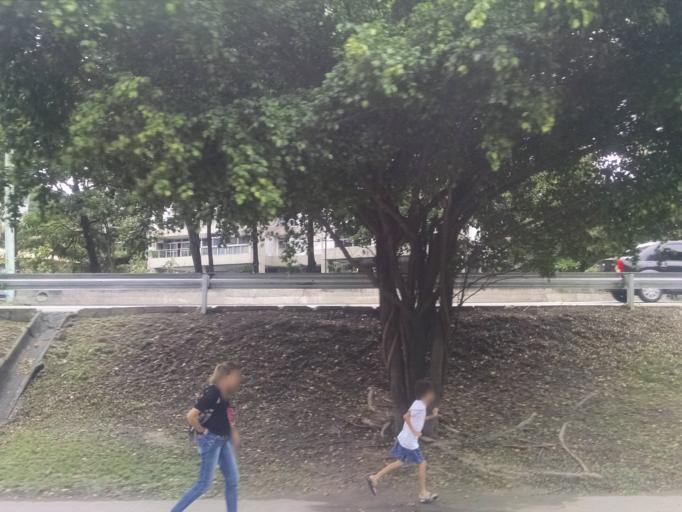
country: BR
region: Rio de Janeiro
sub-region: Rio De Janeiro
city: Rio de Janeiro
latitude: -22.9939
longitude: -43.2560
